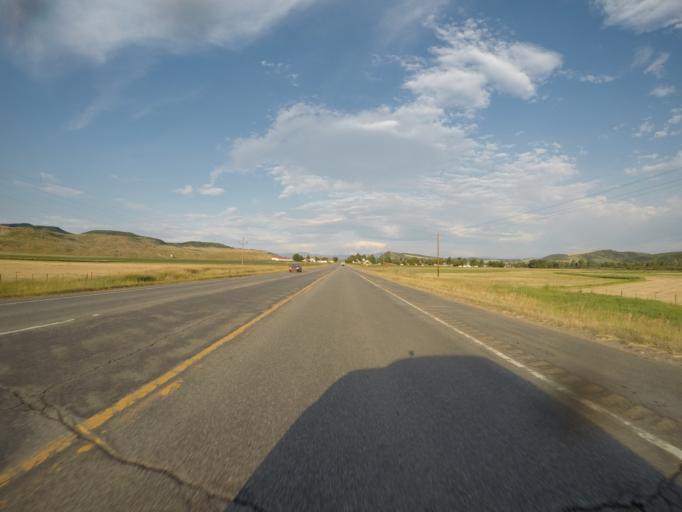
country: US
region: Colorado
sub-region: Routt County
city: Steamboat Springs
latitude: 40.4857
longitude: -107.0289
